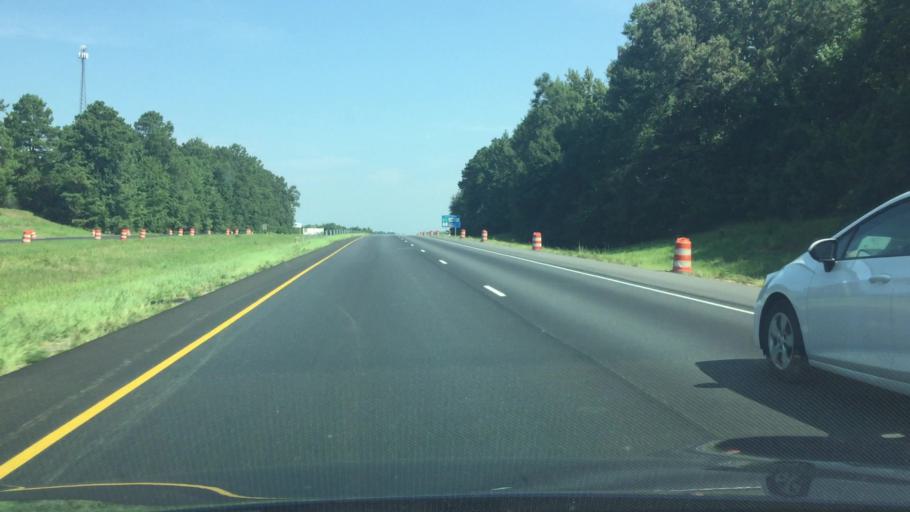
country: US
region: Alabama
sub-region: Chilton County
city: Clanton
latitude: 32.7906
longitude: -86.5760
